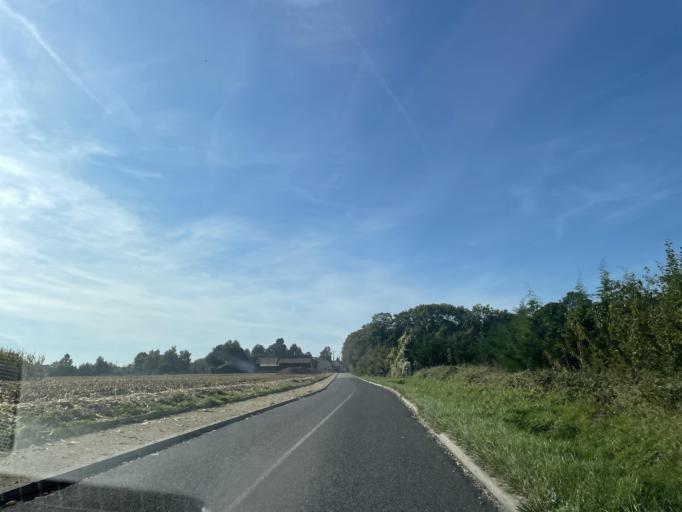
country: FR
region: Ile-de-France
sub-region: Departement de Seine-et-Marne
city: Saint-Jean-les-Deux-Jumeaux
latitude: 48.9463
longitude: 2.9910
